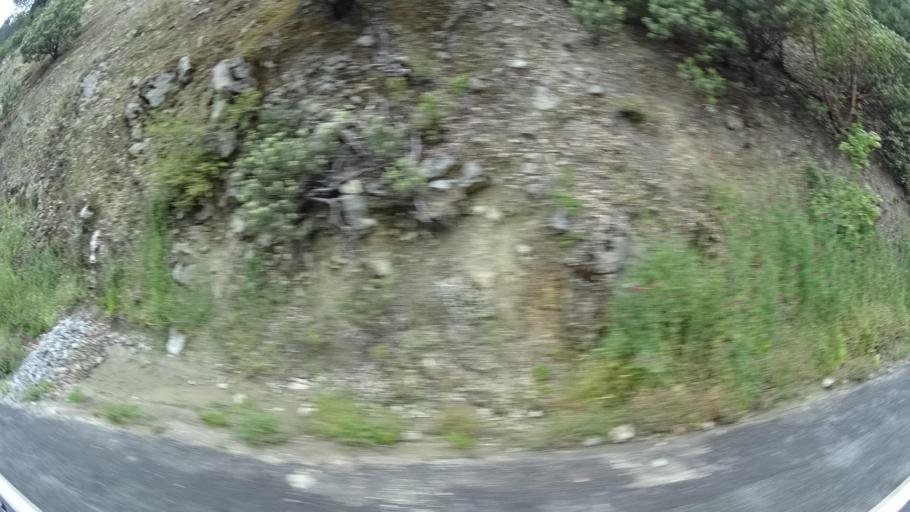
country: US
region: California
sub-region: Humboldt County
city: Willow Creek
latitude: 41.2559
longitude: -123.6258
